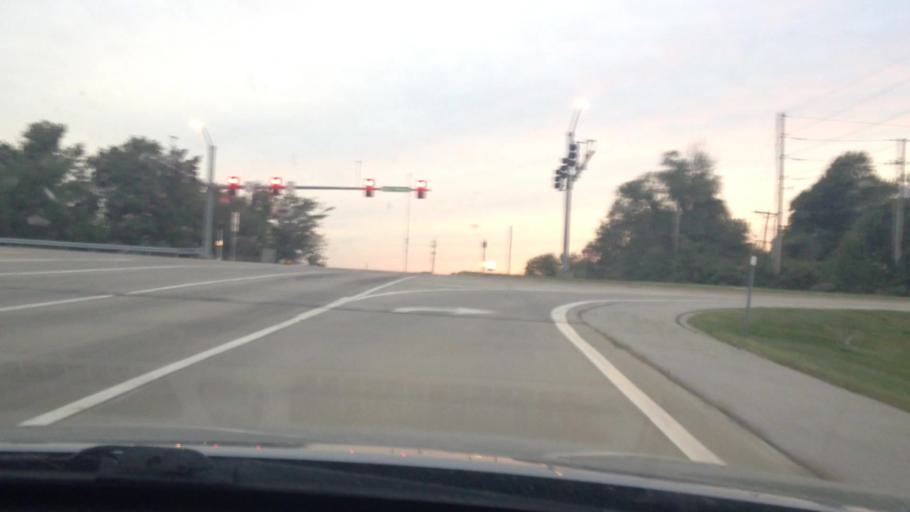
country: US
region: Missouri
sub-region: Jackson County
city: Lees Summit
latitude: 38.9368
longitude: -94.4032
